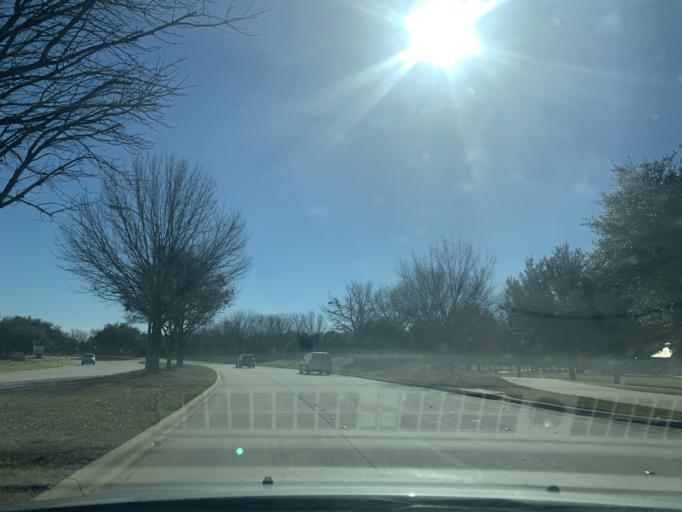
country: US
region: Texas
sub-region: Denton County
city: The Colony
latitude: 33.0543
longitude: -96.8343
